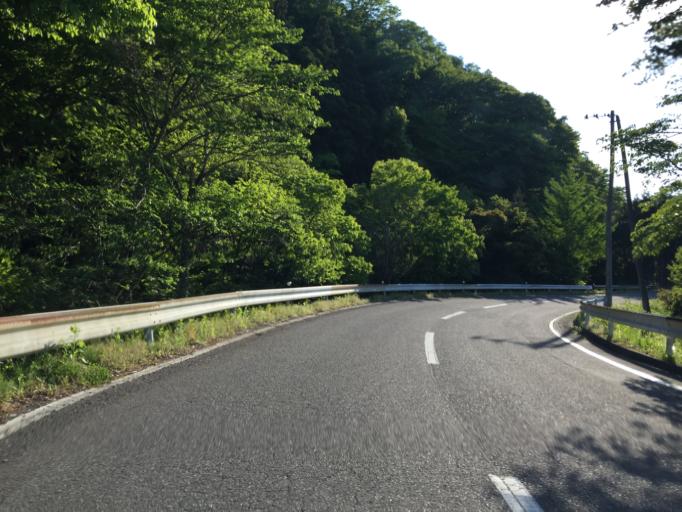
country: JP
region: Ibaraki
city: Daigo
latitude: 36.9209
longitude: 140.5267
